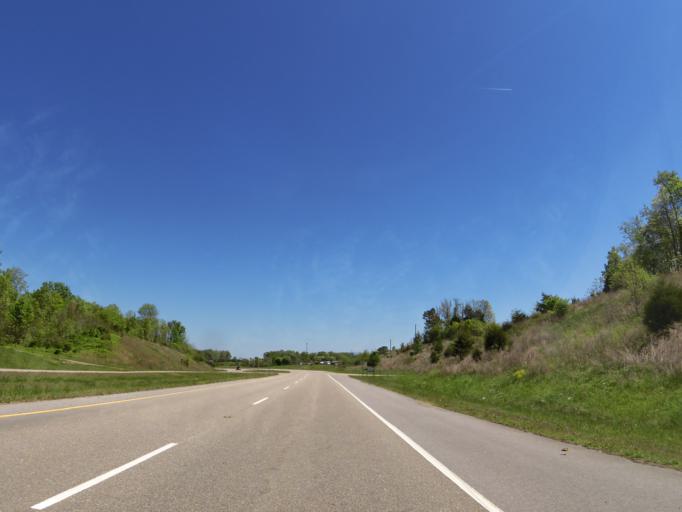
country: US
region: Tennessee
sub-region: Greene County
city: Mosheim
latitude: 36.0365
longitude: -83.0091
